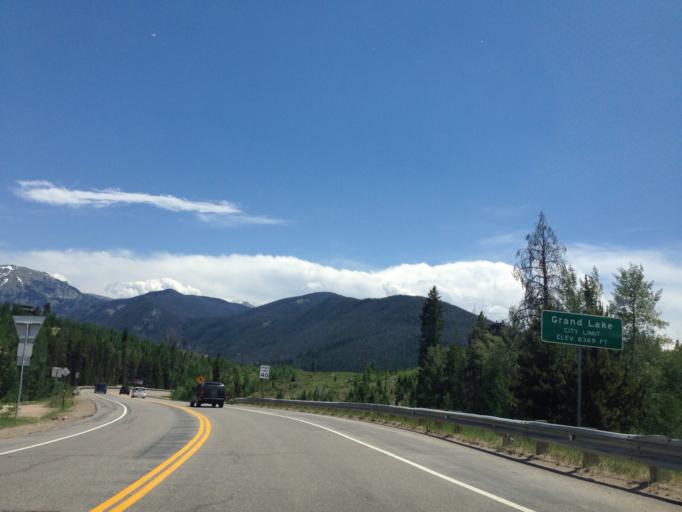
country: US
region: Colorado
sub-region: Grand County
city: Granby
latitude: 40.2563
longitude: -105.8379
